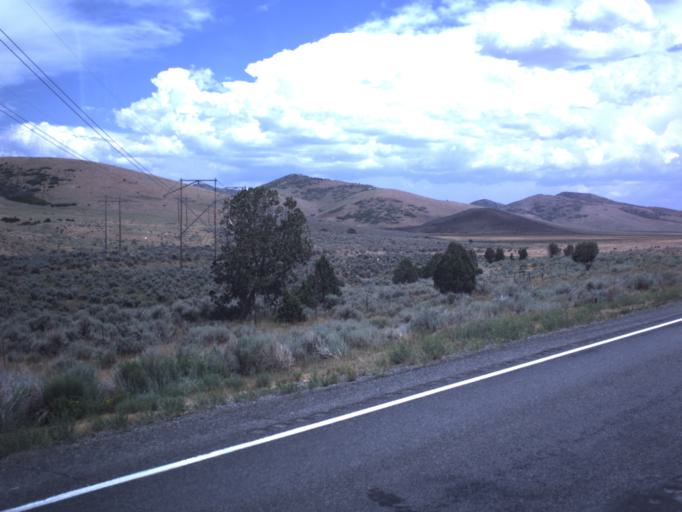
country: US
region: Utah
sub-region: Sanpete County
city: Fountain Green
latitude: 39.6917
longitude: -111.6871
